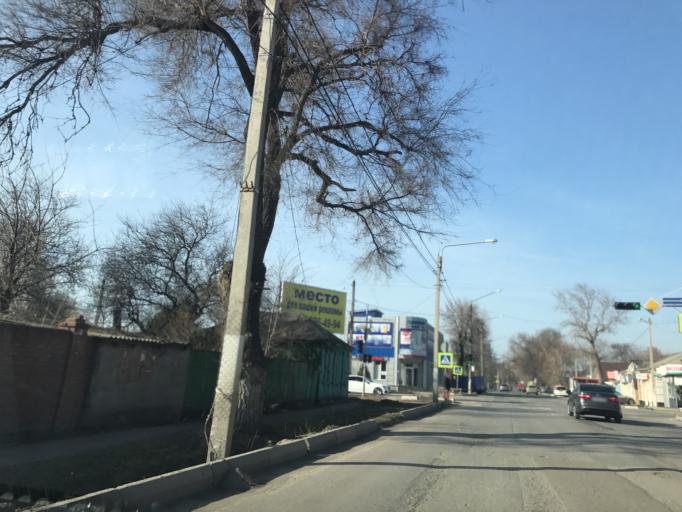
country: RU
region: Rostov
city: Bataysk
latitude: 47.1418
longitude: 39.7498
